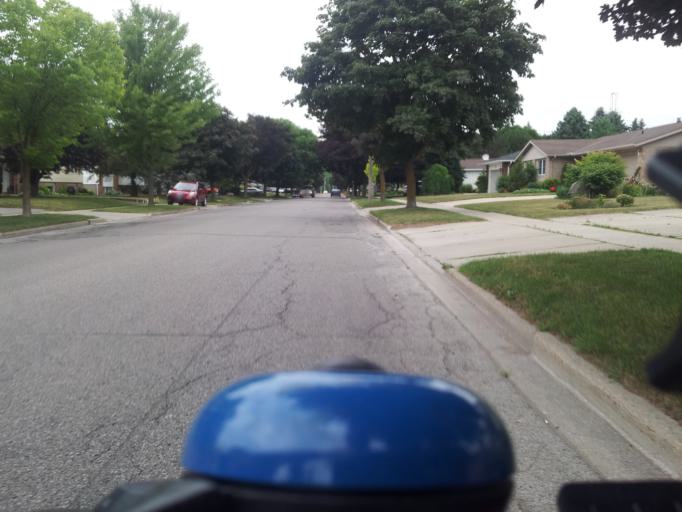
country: CA
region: Ontario
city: Stratford
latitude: 43.3749
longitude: -80.9514
